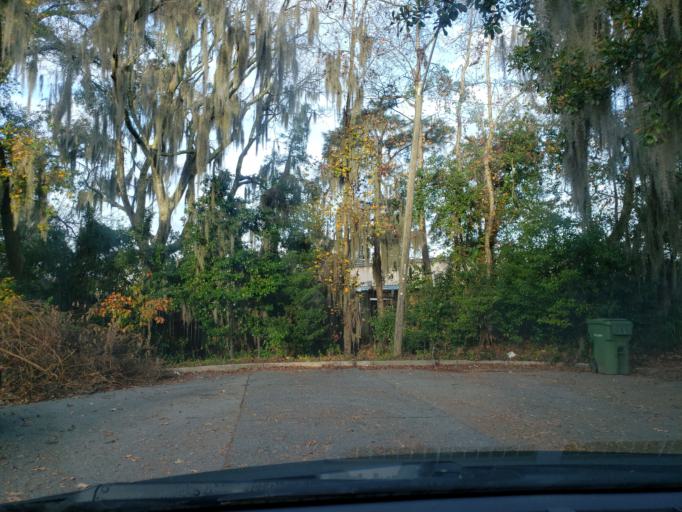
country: US
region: Georgia
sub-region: Chatham County
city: Montgomery
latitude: 31.9950
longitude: -81.1232
